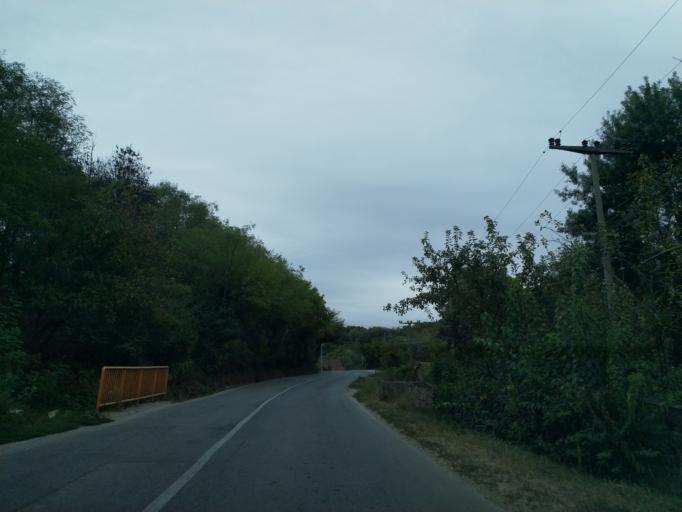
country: RS
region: Central Serbia
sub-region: Pomoravski Okrug
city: Jagodina
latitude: 44.0426
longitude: 21.1861
